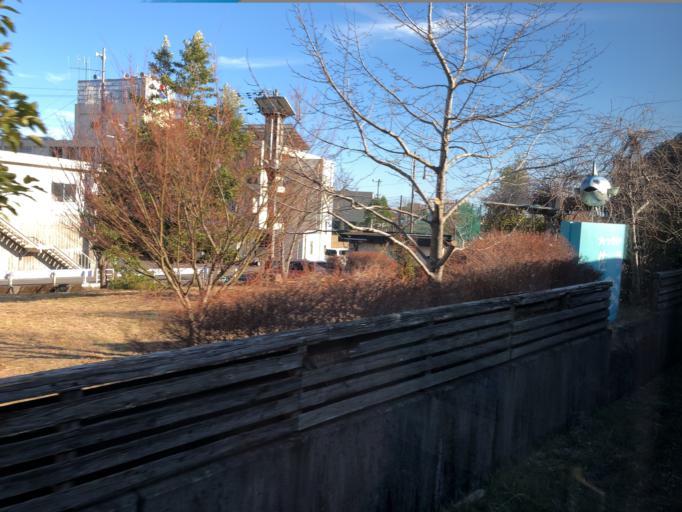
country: JP
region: Kochi
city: Nakamura
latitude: 33.0806
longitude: 133.1016
